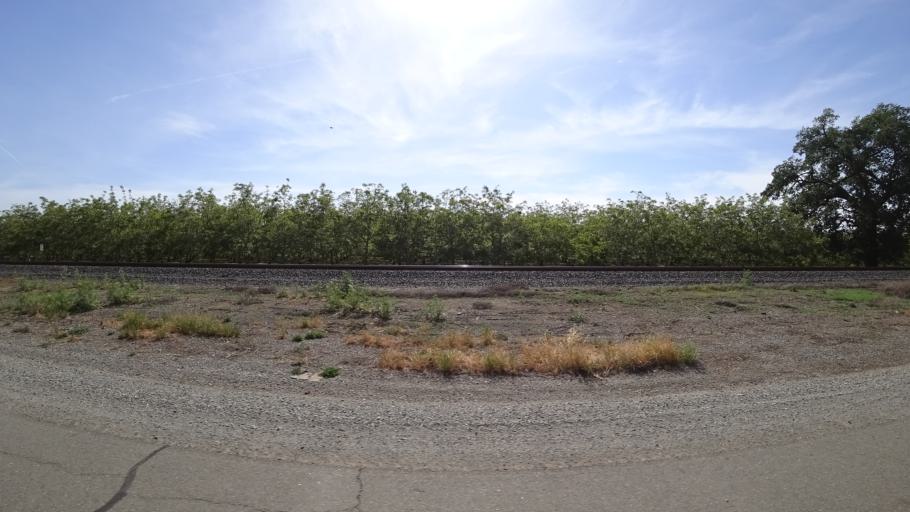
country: US
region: California
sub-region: Tehama County
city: Los Molinos
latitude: 39.9915
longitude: -122.0849
